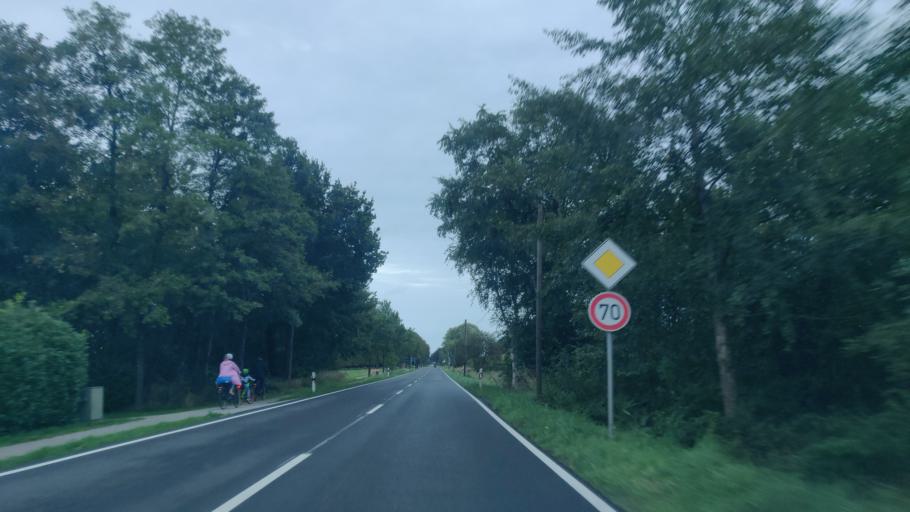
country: DE
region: Lower Saxony
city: Aurich
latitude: 53.4843
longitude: 7.4228
